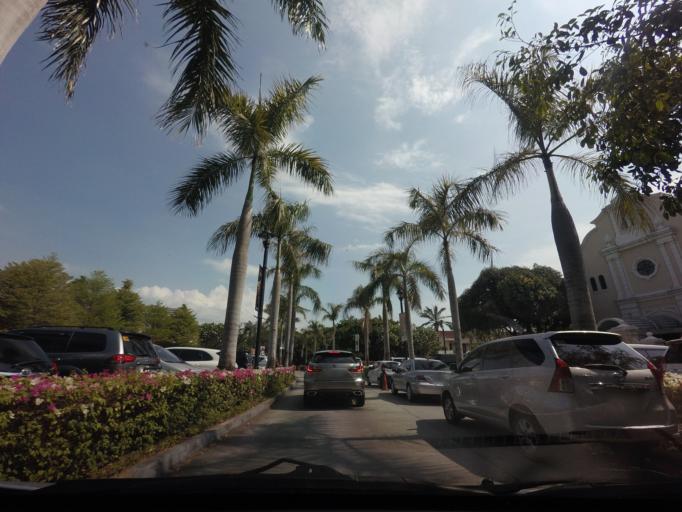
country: PH
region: Metro Manila
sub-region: Makati City
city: Makati City
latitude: 14.5475
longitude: 121.0343
